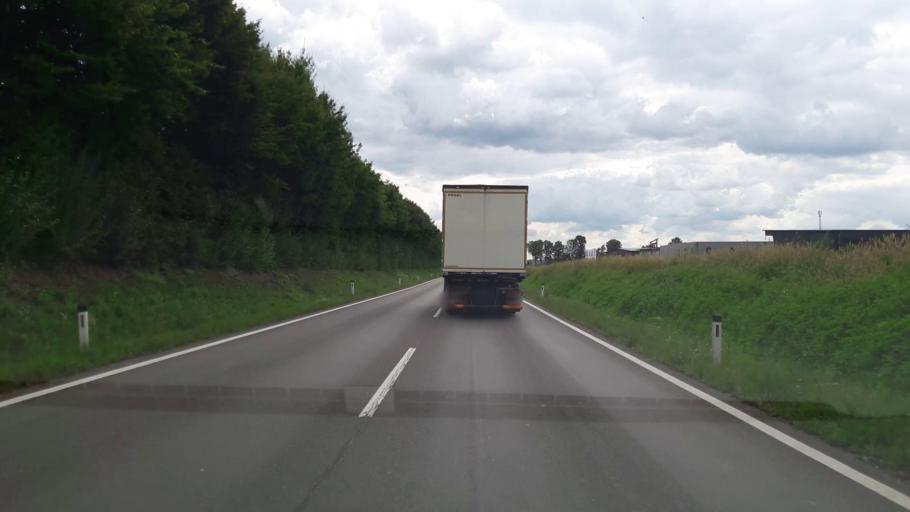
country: AT
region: Styria
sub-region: Politischer Bezirk Weiz
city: Gleisdorf
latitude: 47.1254
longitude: 15.6929
